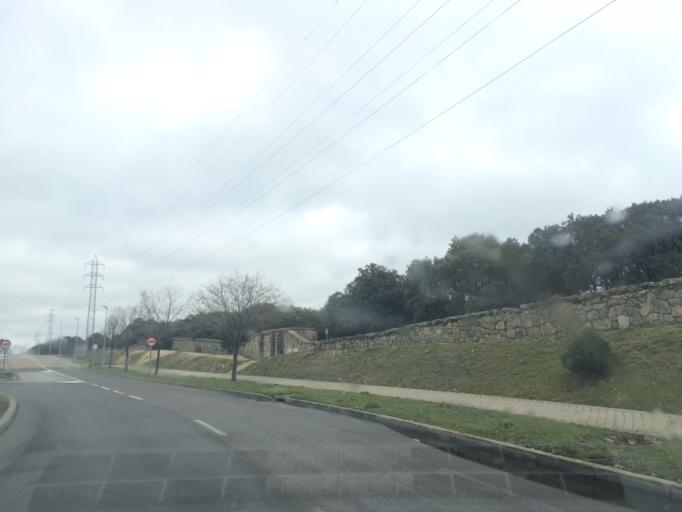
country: ES
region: Madrid
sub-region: Provincia de Madrid
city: Tres Cantos
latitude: 40.5932
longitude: -3.6947
